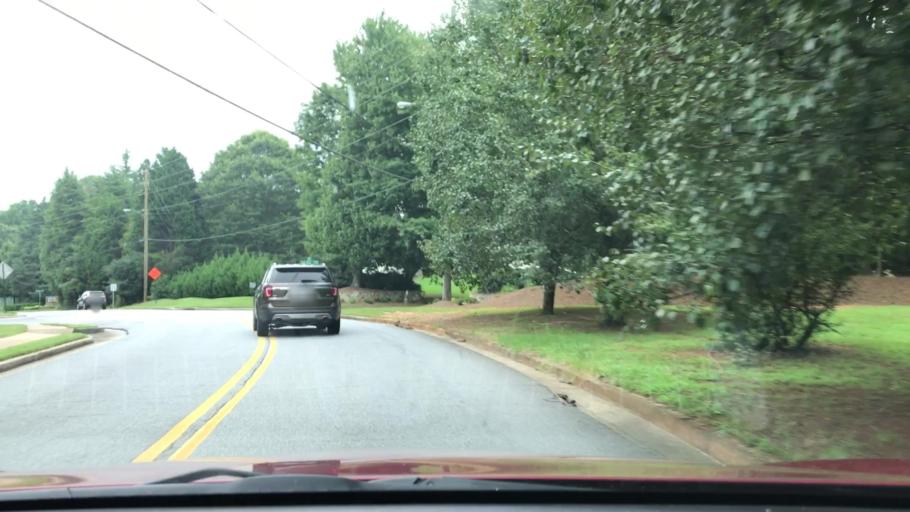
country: US
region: Georgia
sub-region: Gwinnett County
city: Suwanee
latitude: 34.0057
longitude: -84.0301
